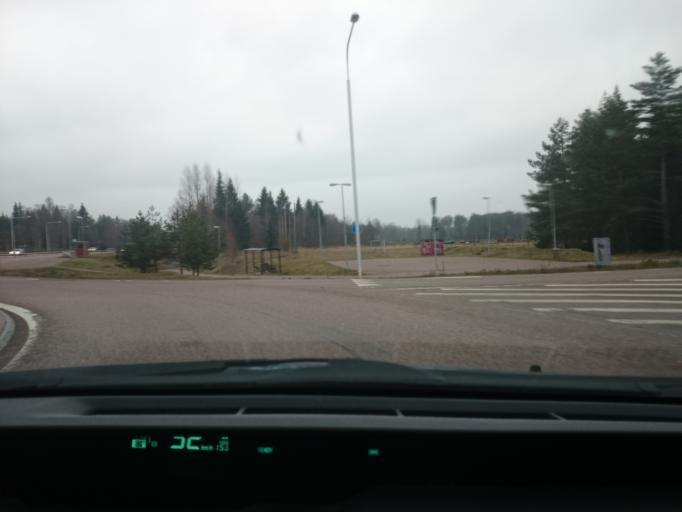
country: SE
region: Dalarna
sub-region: Saters Kommun
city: Saeter
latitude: 60.3381
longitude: 15.7793
